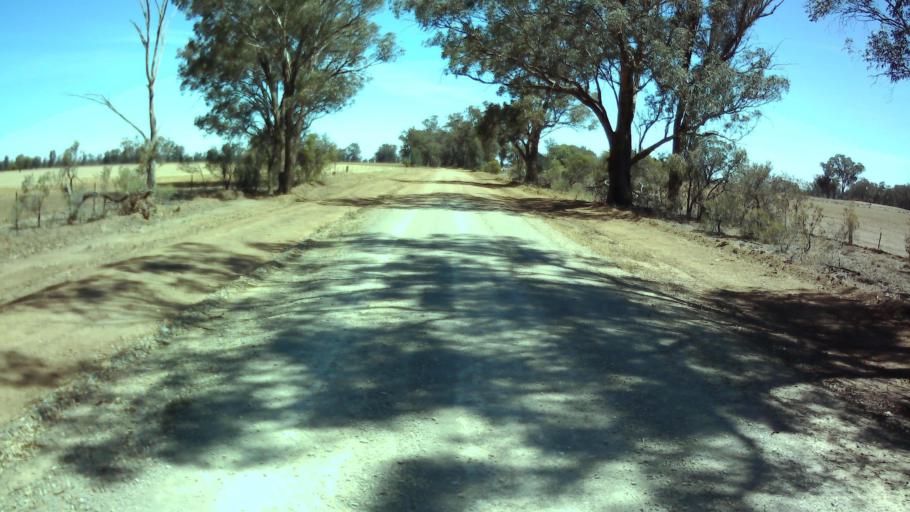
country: AU
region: New South Wales
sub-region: Bland
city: West Wyalong
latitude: -33.9107
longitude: 147.6846
